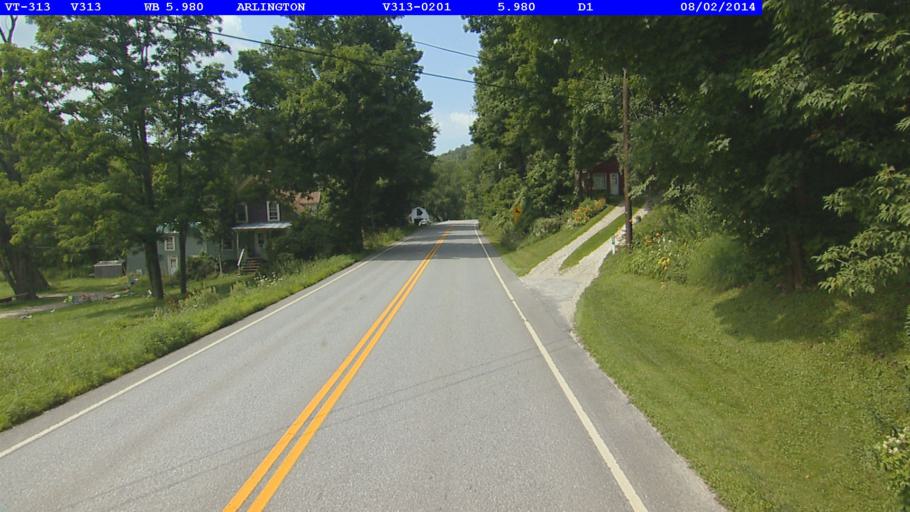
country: US
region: Vermont
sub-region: Bennington County
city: Arlington
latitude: 43.0764
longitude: -73.1656
